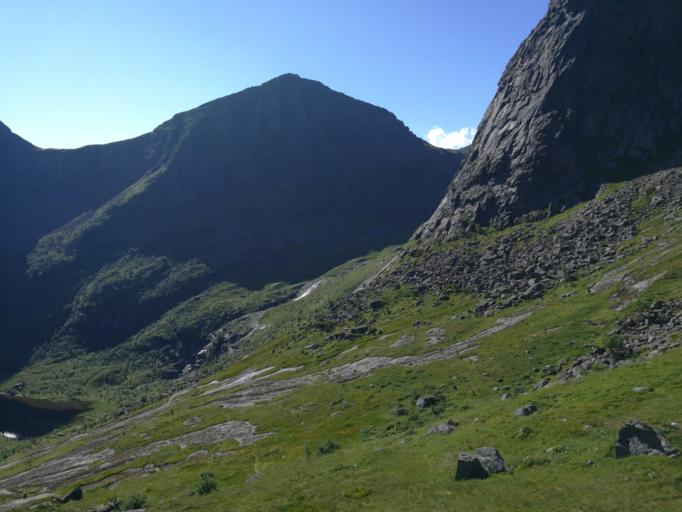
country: NO
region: Nordland
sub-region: Moskenes
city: Reine
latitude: 67.9243
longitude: 13.0417
